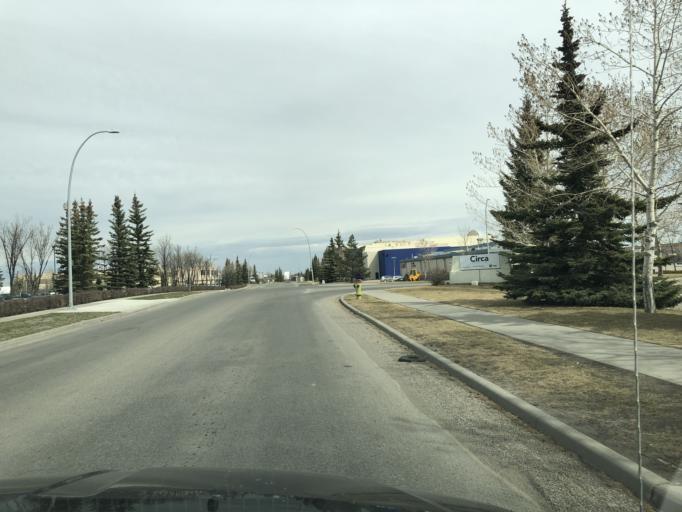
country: CA
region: Alberta
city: Calgary
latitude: 51.0722
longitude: -113.9918
